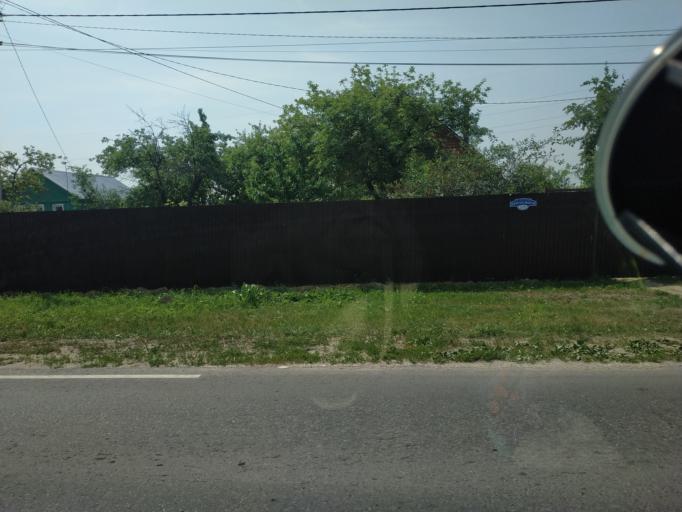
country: RU
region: Moskovskaya
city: Malyshevo
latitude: 55.5021
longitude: 38.3270
